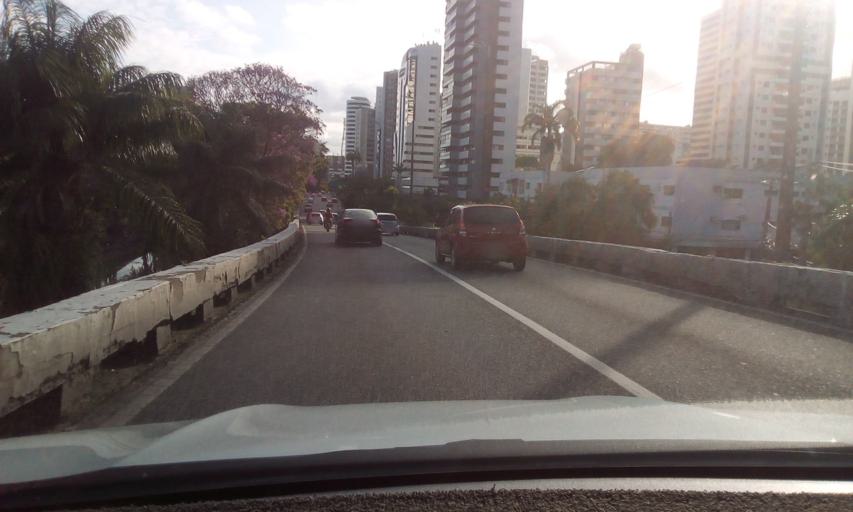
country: BR
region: Pernambuco
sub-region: Recife
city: Recife
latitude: -8.0452
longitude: -34.8903
